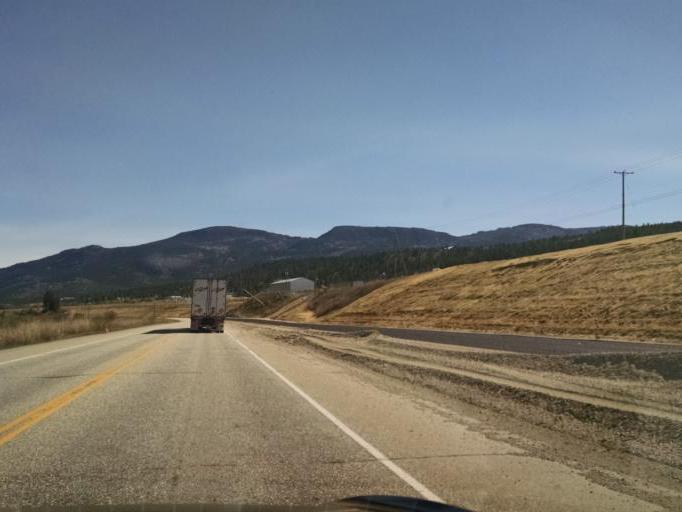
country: CA
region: British Columbia
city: Chase
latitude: 50.6724
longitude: -119.8420
